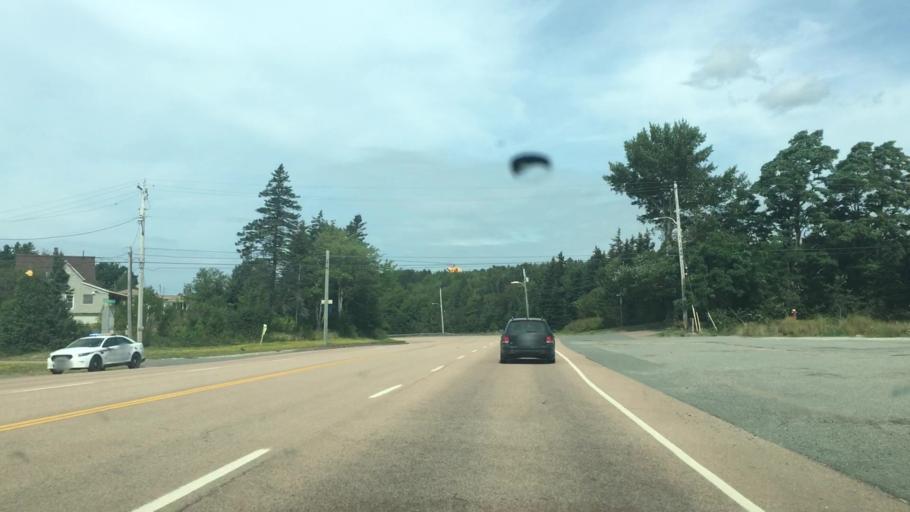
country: CA
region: Nova Scotia
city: Port Hawkesbury
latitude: 45.6232
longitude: -61.3649
